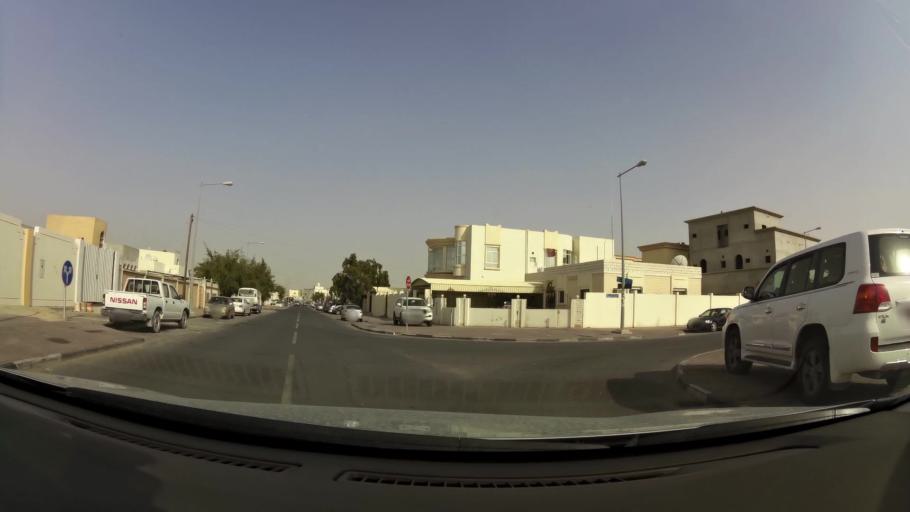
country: QA
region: Baladiyat ar Rayyan
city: Ar Rayyan
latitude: 25.2389
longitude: 51.4365
